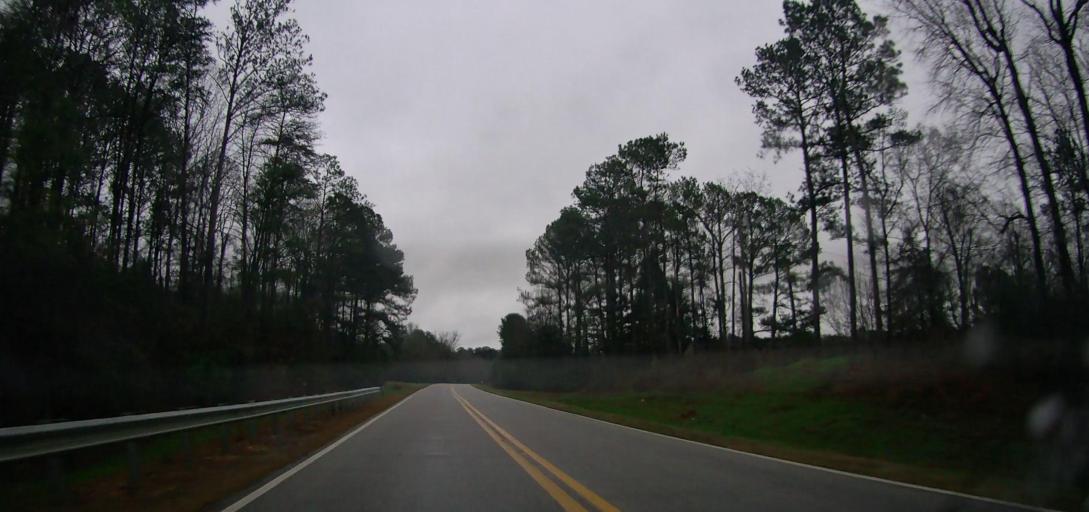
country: US
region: Alabama
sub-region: Bibb County
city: Centreville
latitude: 32.9053
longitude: -87.0094
